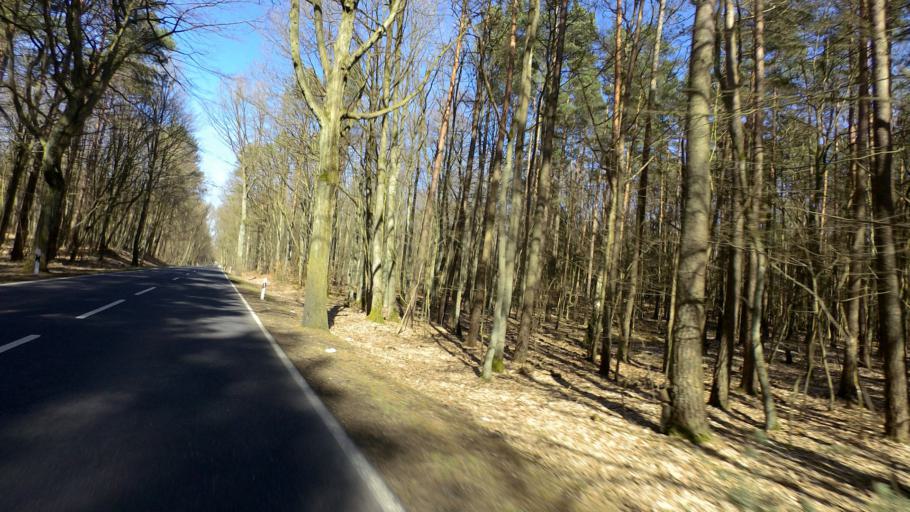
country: DE
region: Brandenburg
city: Werftpfuhl
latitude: 52.6709
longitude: 13.8301
